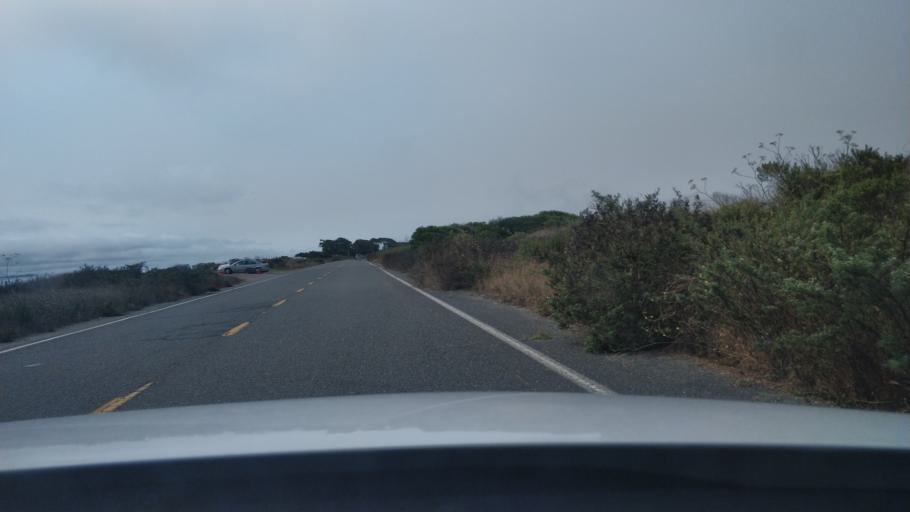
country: US
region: California
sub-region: Humboldt County
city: Bayview
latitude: 40.7760
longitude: -124.2109
